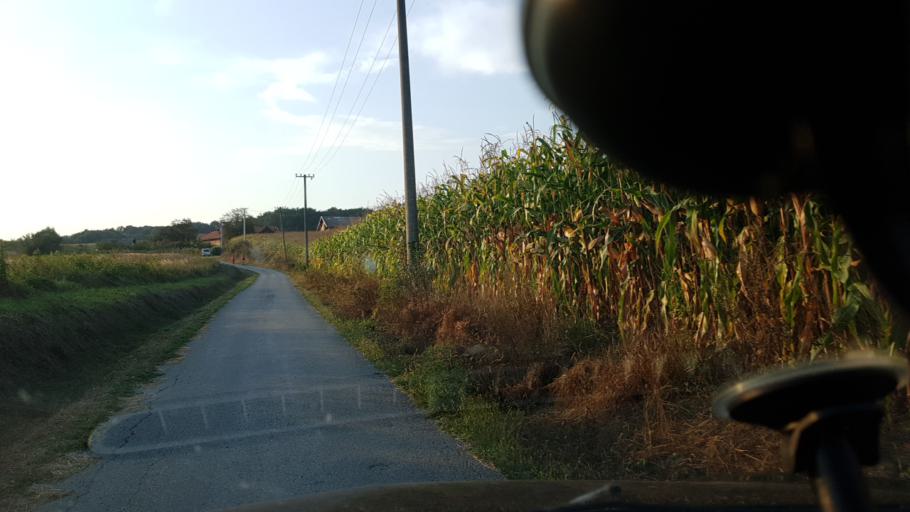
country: HR
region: Krapinsko-Zagorska
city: Selnica
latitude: 46.0586
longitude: 16.0411
